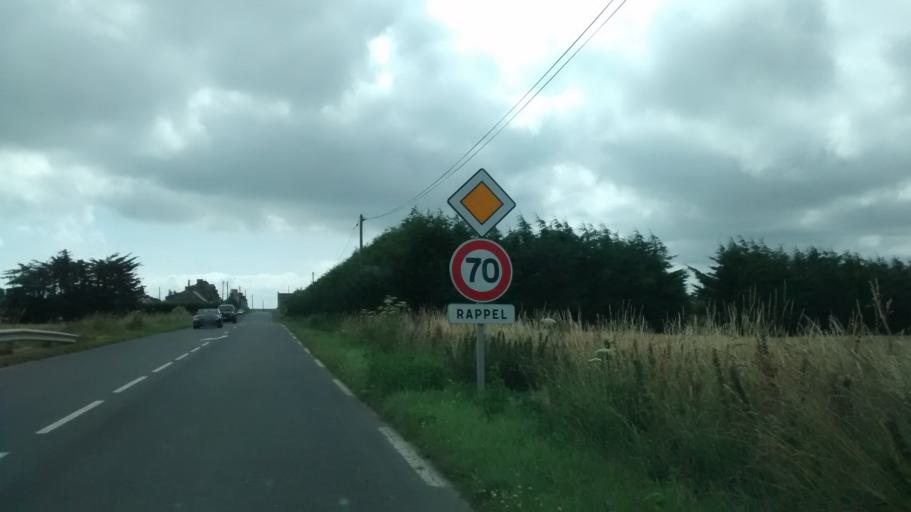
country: FR
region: Brittany
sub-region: Departement d'Ille-et-Vilaine
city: Saint-Meloir-des-Ondes
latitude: 48.6474
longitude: -1.9025
